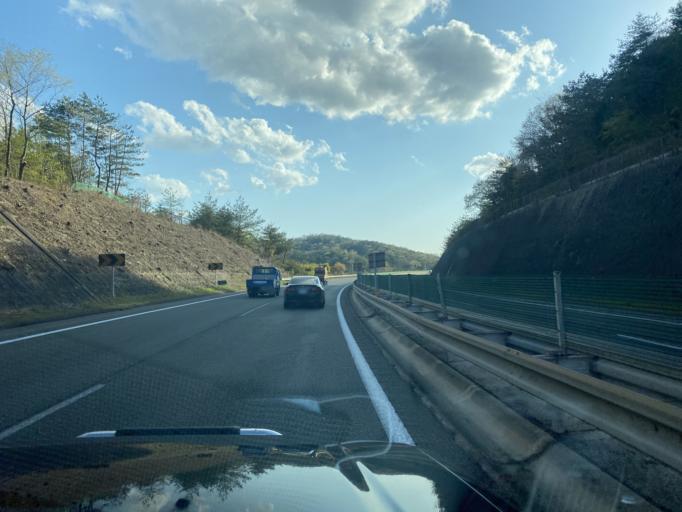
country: JP
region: Hyogo
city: Sandacho
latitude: 34.9679
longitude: 135.1454
